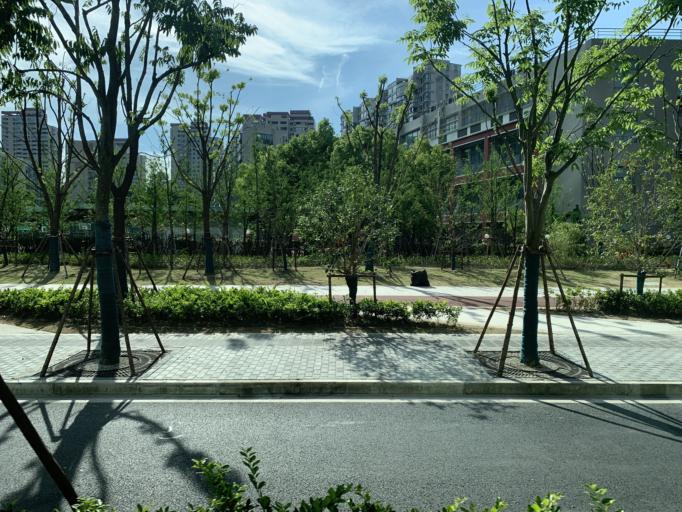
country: CN
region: Shanghai Shi
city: Huamu
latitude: 31.2156
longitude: 121.5295
